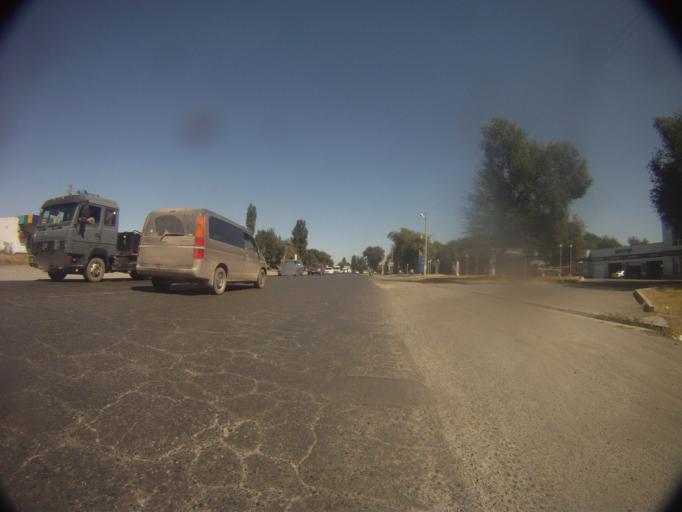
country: KG
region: Chuy
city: Sokuluk
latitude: 42.8647
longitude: 74.3410
